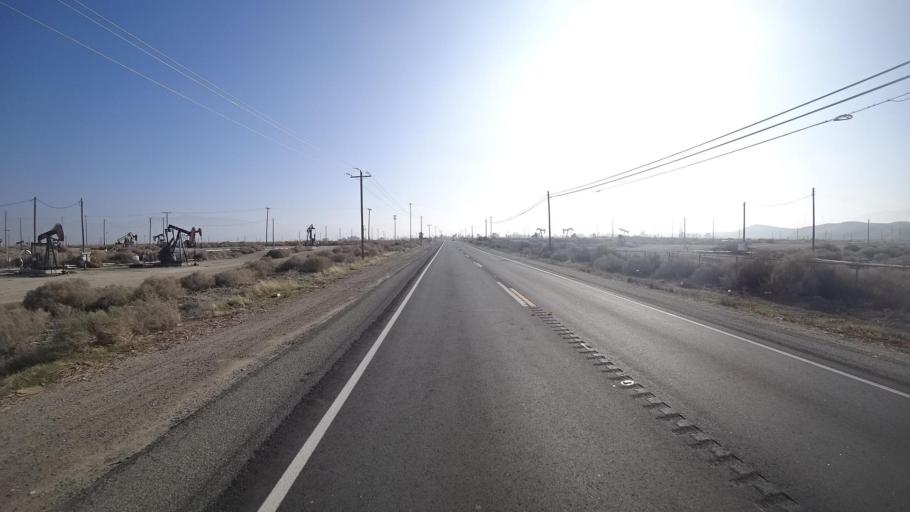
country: US
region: California
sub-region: Kern County
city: Maricopa
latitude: 35.0705
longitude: -119.4020
